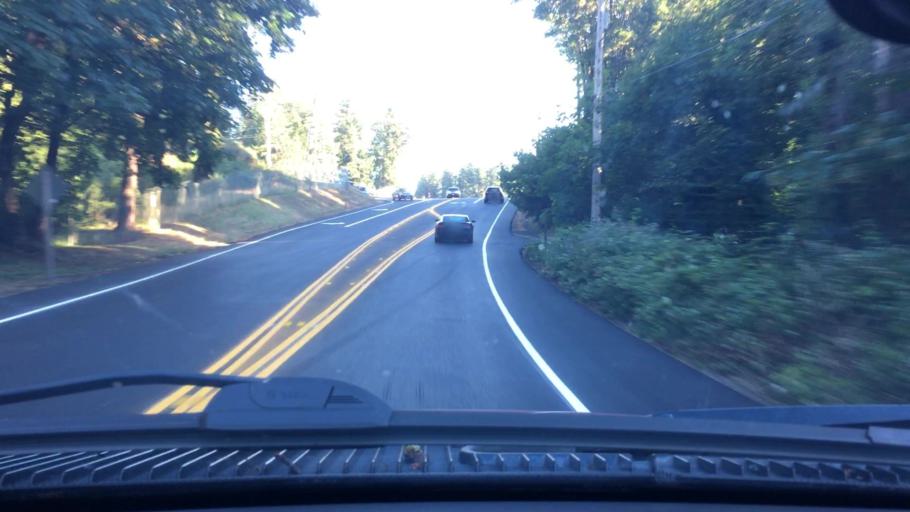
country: US
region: Washington
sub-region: King County
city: Maple Valley
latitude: 47.3447
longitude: -122.0537
